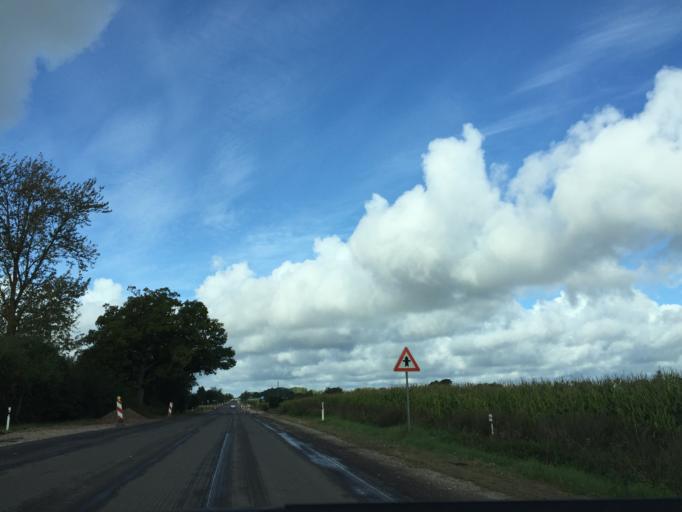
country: LV
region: Engure
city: Smarde
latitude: 56.9230
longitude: 23.2464
